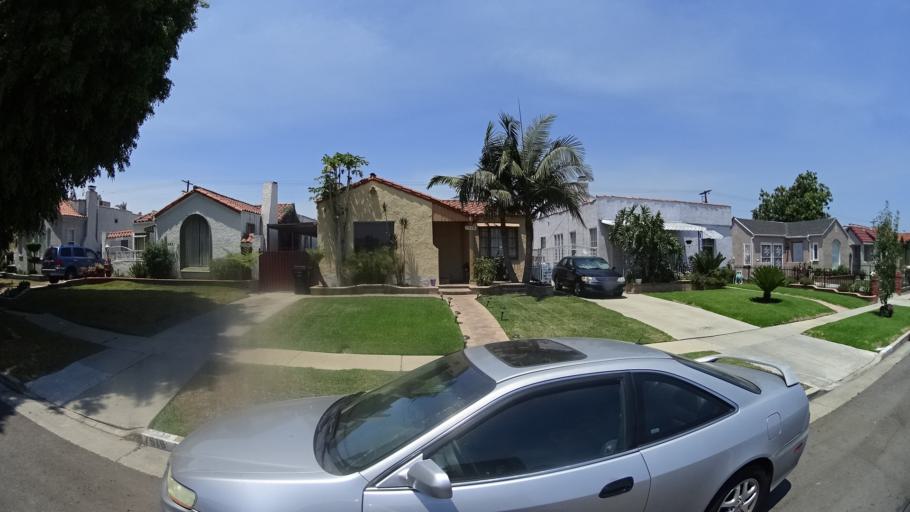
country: US
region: California
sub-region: Los Angeles County
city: Westmont
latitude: 33.9716
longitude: -118.3035
